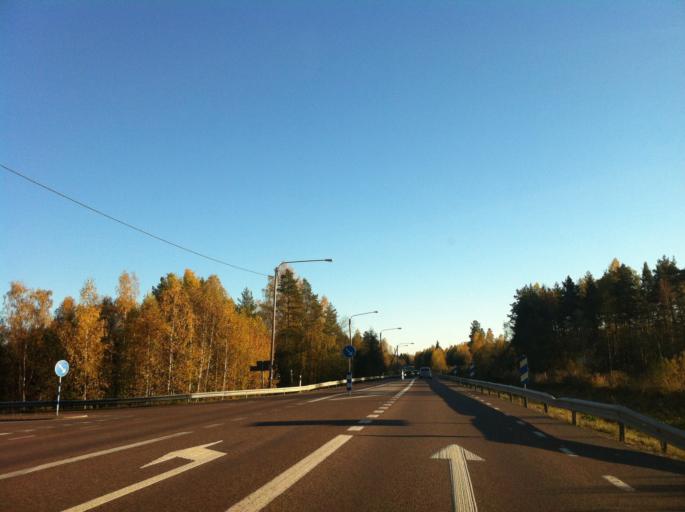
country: SE
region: Dalarna
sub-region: Faluns Kommun
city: Grycksbo
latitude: 60.6637
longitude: 15.5464
